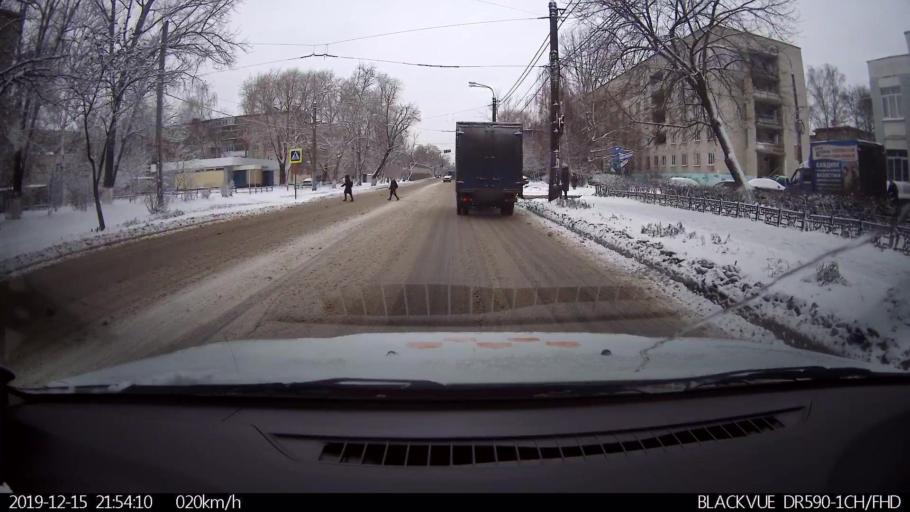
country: RU
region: Nizjnij Novgorod
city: Burevestnik
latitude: 56.2337
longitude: 43.8775
